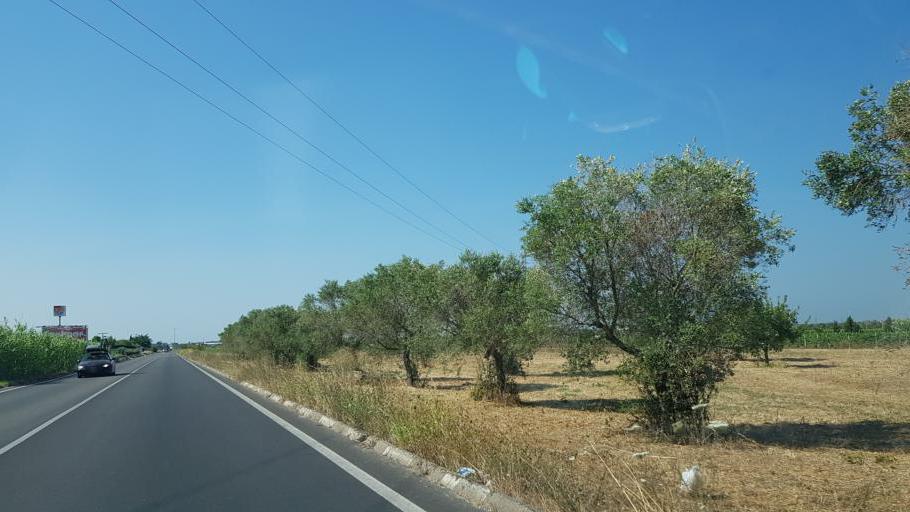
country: IT
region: Apulia
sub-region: Provincia di Lecce
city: Veglie
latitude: 40.3576
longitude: 17.9681
